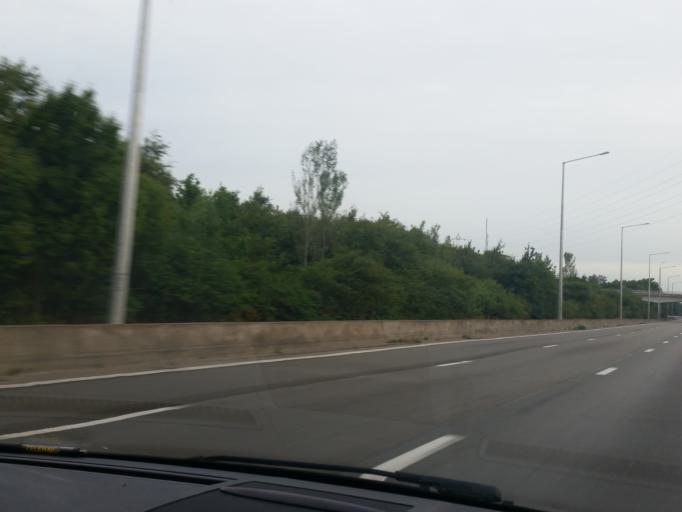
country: BE
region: Flanders
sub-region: Provincie Antwerpen
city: Mechelen
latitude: 51.0507
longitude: 4.4535
